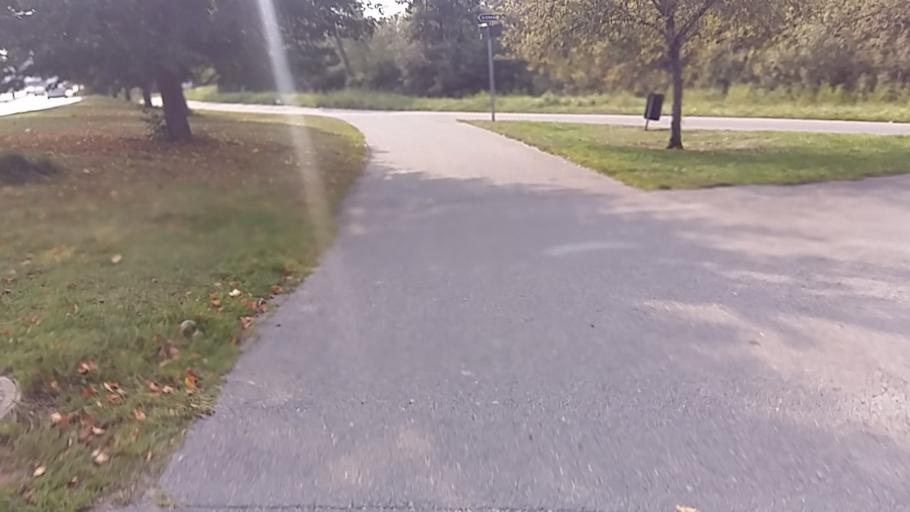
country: SE
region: Joenkoeping
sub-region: Jonkopings Kommun
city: Jonkoping
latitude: 57.7672
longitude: 14.1532
